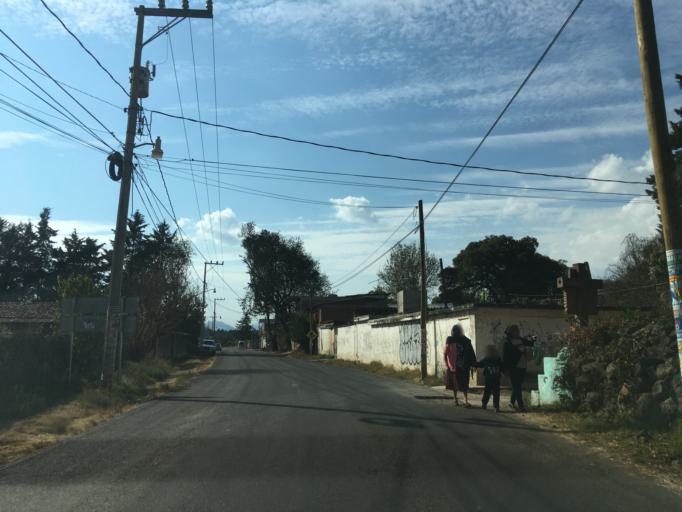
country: MX
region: Michoacan
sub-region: Patzcuaro
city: Santa Ana Chapitiro
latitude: 19.5383
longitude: -101.6341
